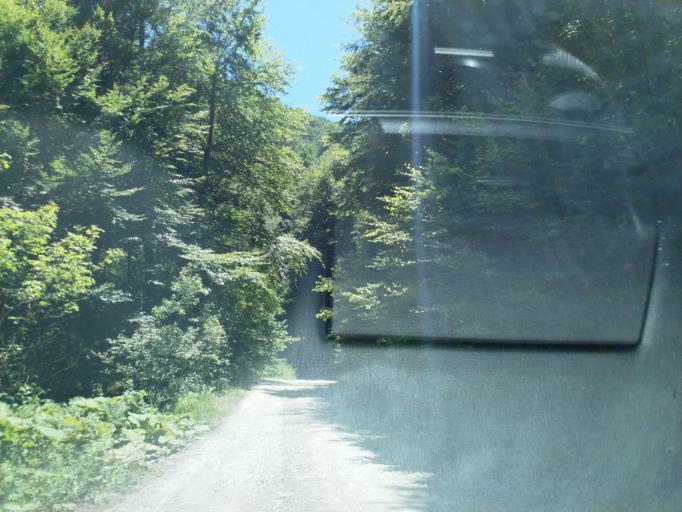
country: XK
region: Mitrovica
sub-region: Komuna e Leposaviqit
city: Leposaviq
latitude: 43.2766
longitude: 20.8685
